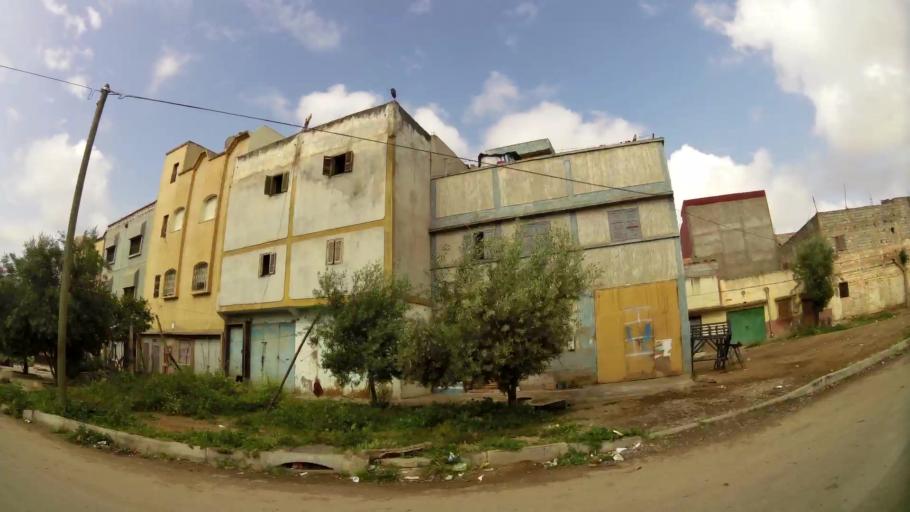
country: MA
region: Rabat-Sale-Zemmour-Zaer
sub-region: Khemisset
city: Tiflet
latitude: 33.8903
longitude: -6.3053
